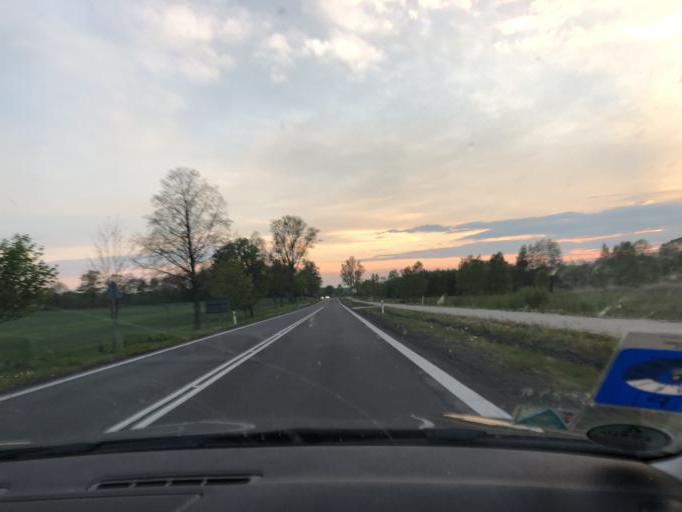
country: PL
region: Lubusz
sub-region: Powiat zarski
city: Trzebiel
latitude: 51.6326
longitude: 14.8323
